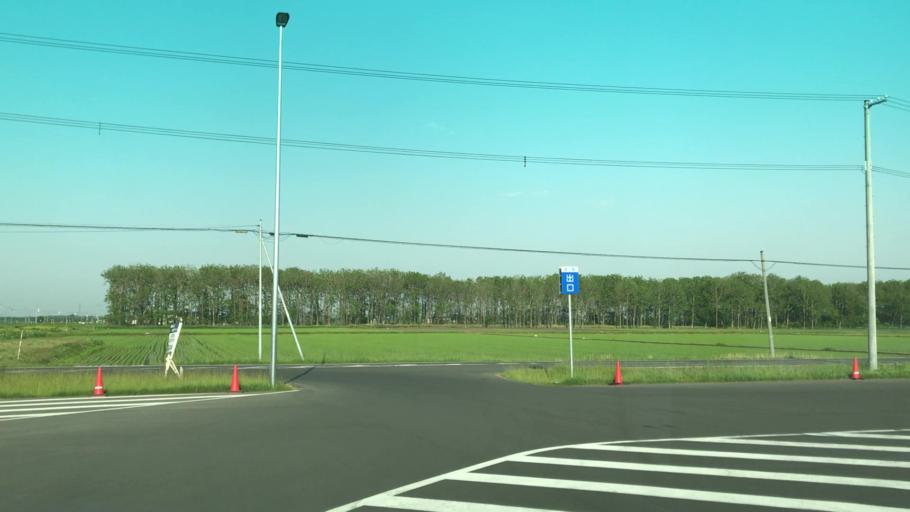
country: JP
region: Hokkaido
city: Tobetsu
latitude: 43.1776
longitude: 141.4492
